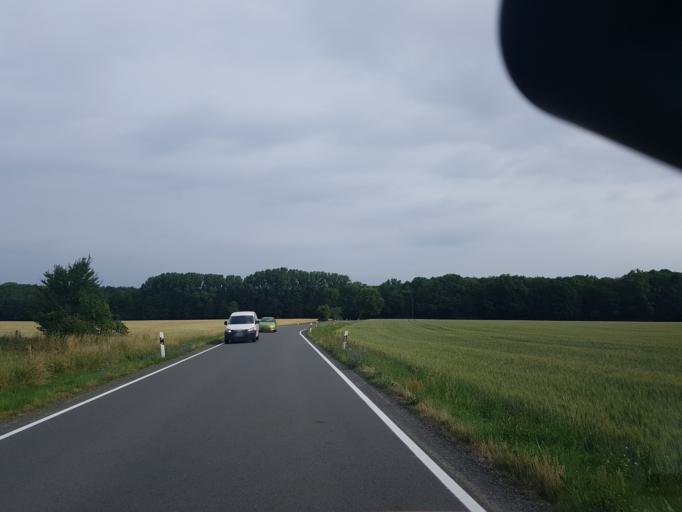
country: DE
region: Brandenburg
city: Sonnewalde
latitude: 51.6937
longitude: 13.6249
